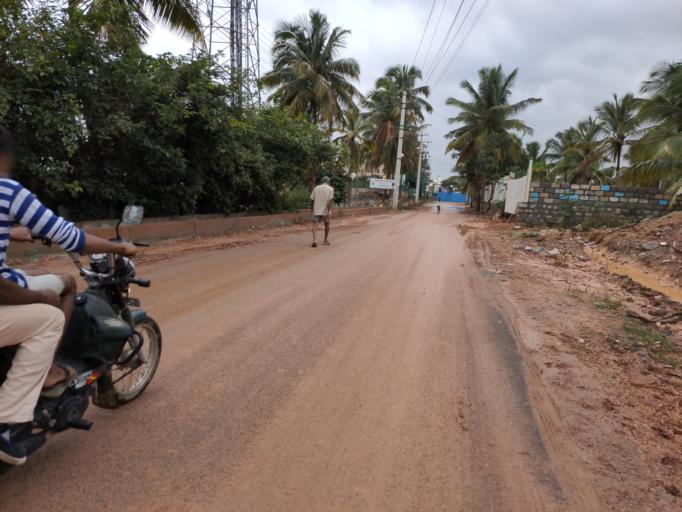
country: IN
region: Karnataka
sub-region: Bangalore Rural
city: Hoskote
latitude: 13.0085
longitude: 77.7604
